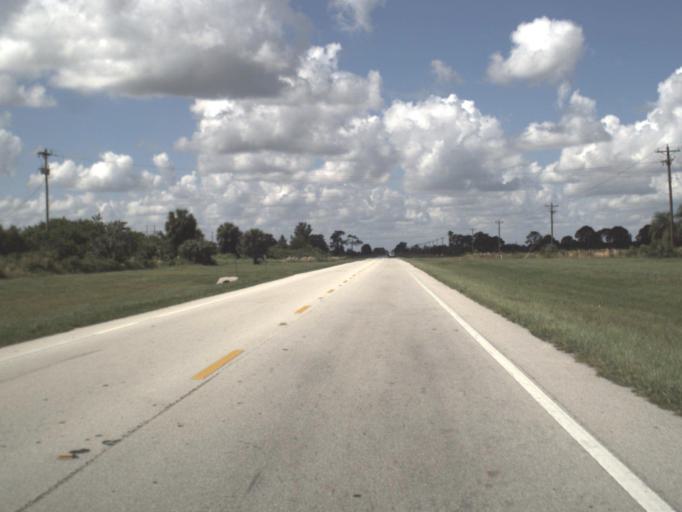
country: US
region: Florida
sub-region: Collier County
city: Immokalee
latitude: 26.4926
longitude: -81.4620
